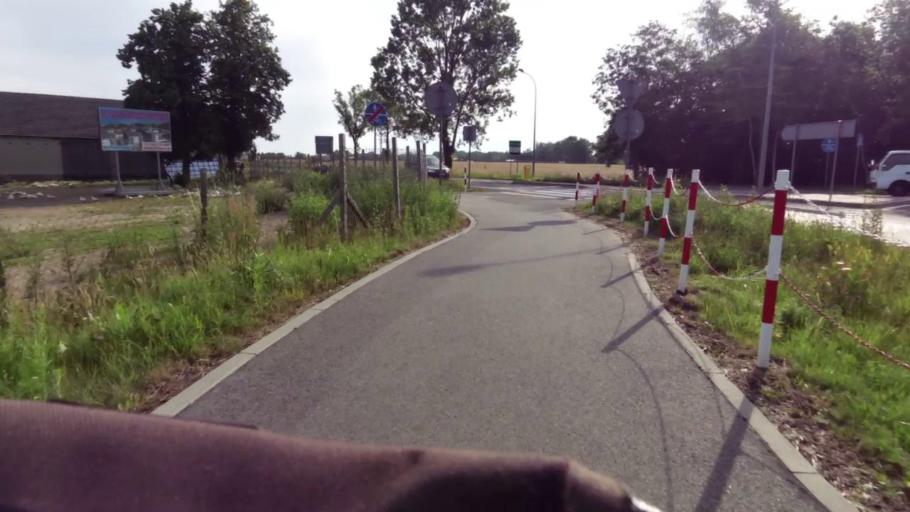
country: PL
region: West Pomeranian Voivodeship
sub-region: Powiat kamienski
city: Kamien Pomorski
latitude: 53.9936
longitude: 14.8159
